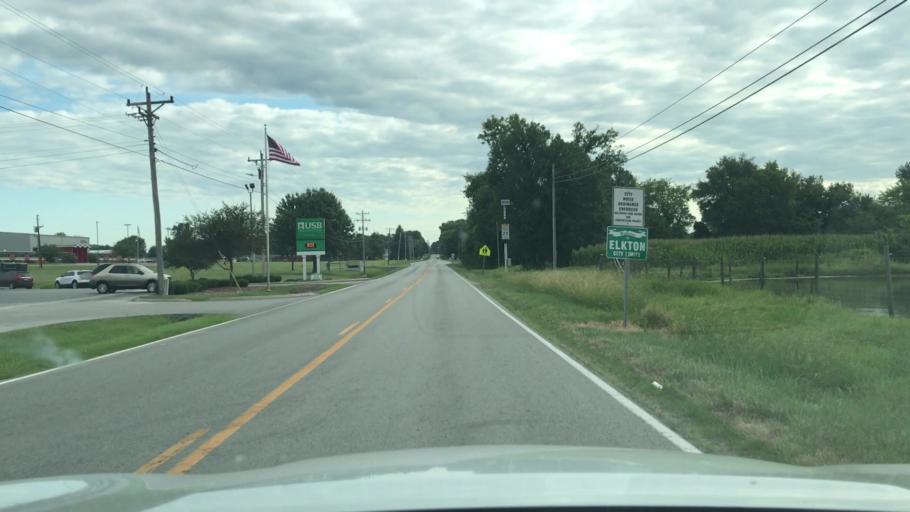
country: US
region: Kentucky
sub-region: Todd County
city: Elkton
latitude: 36.7949
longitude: -87.1615
